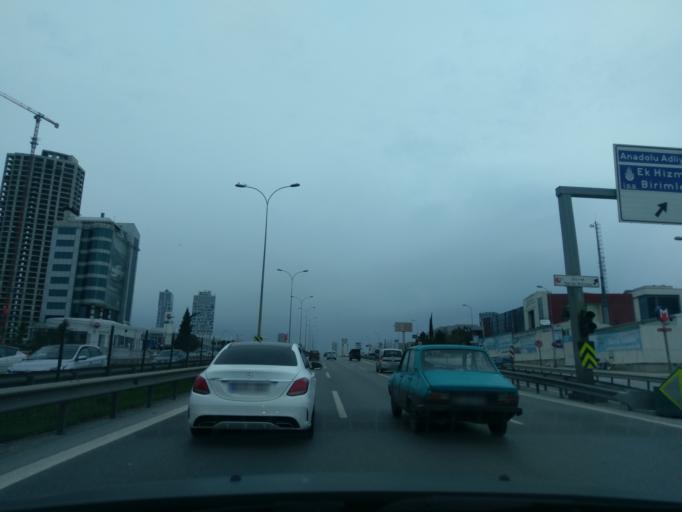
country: TR
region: Istanbul
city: Maltepe
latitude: 40.9176
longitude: 29.1752
